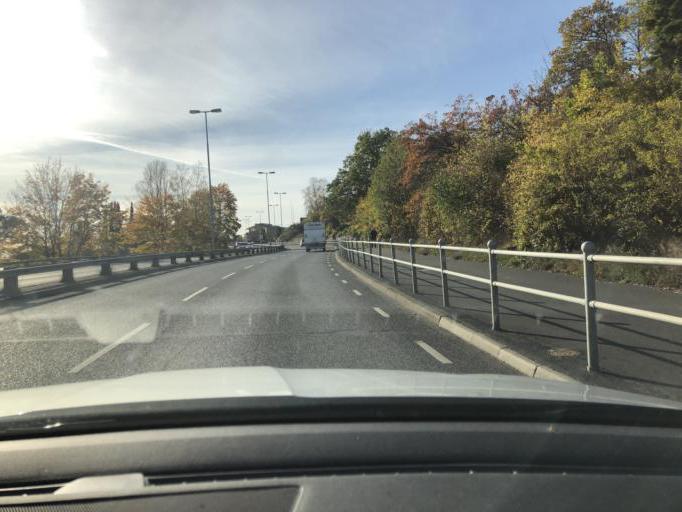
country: SE
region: Joenkoeping
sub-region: Jonkopings Kommun
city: Jonkoping
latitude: 57.7736
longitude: 14.1402
